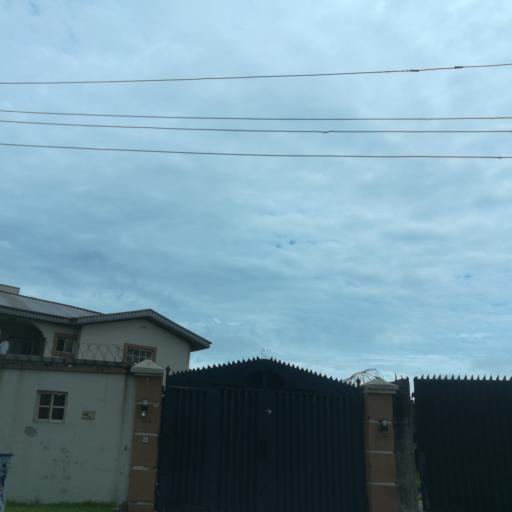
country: NG
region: Lagos
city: Ikoyi
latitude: 6.4383
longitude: 3.4769
